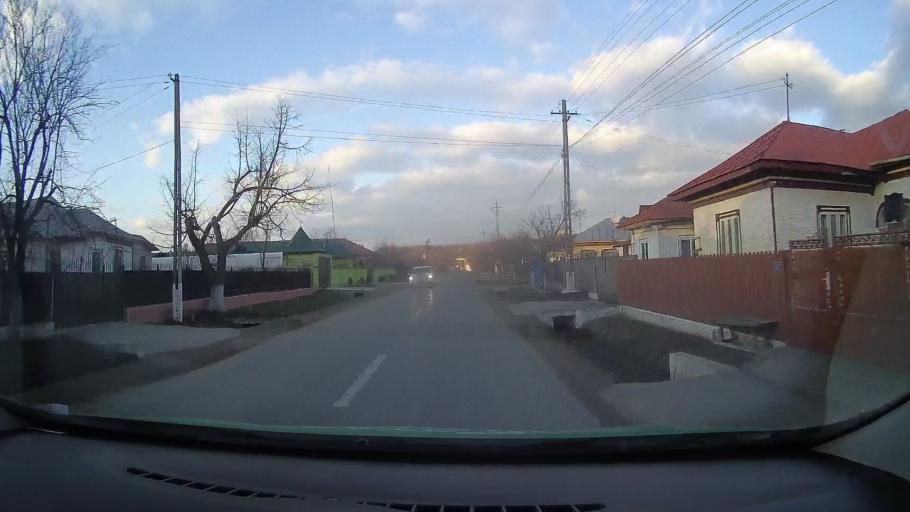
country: RO
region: Dambovita
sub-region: Comuna Gura Ocnitei
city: Adanca
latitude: 44.9139
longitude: 25.6150
